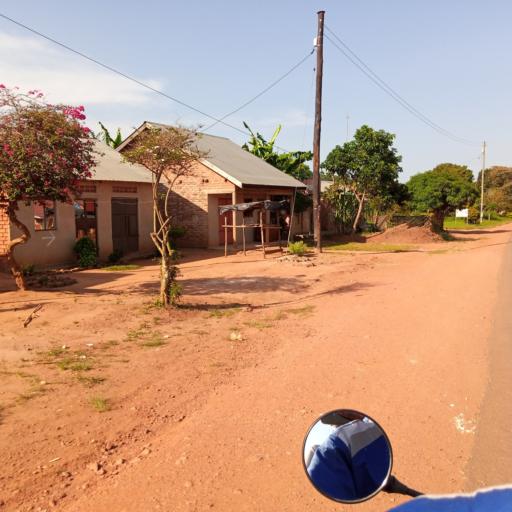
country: UG
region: Central Region
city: Masaka
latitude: -0.4258
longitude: 31.6691
